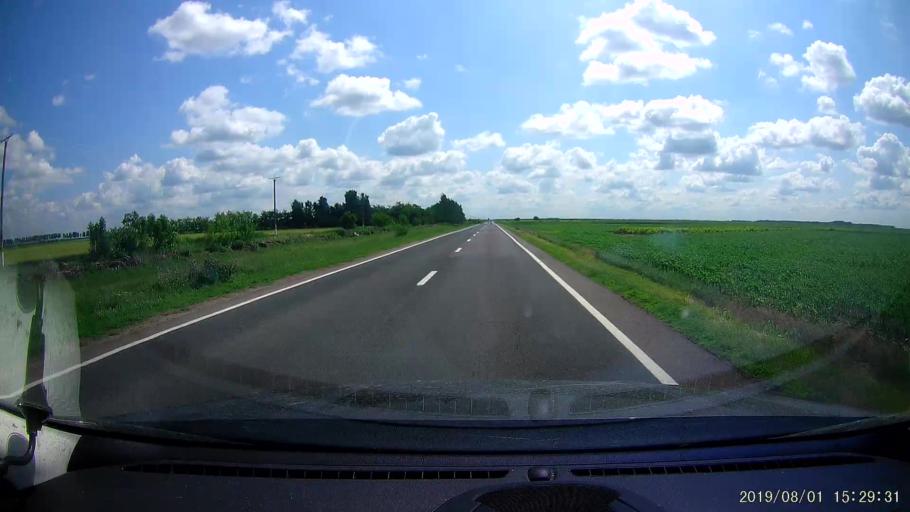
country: RO
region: Braila
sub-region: Comuna Viziru
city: Viziru
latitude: 44.9806
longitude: 27.6954
